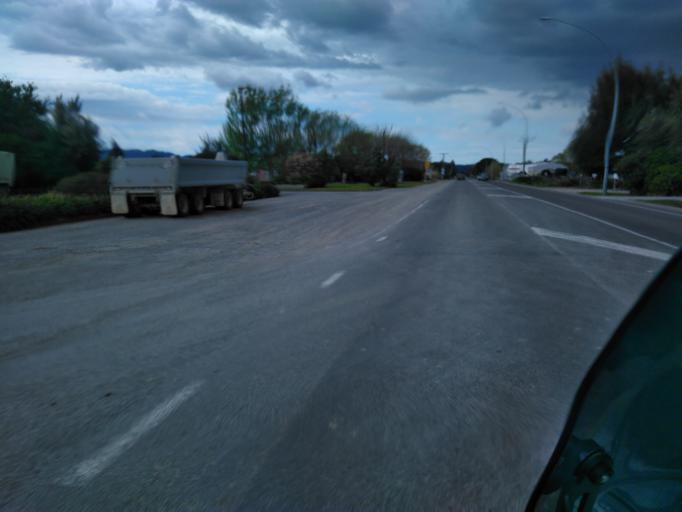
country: NZ
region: Gisborne
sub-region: Gisborne District
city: Gisborne
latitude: -38.6491
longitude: 177.9704
